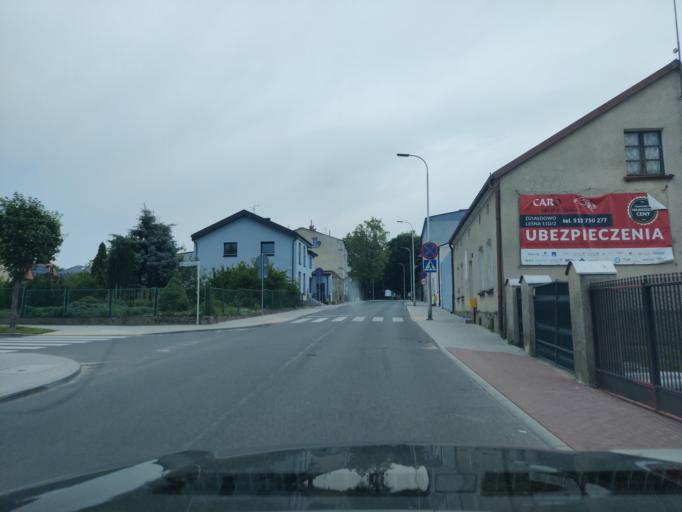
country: PL
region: Warmian-Masurian Voivodeship
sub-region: Powiat dzialdowski
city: Dzialdowo
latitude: 53.2364
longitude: 20.1850
